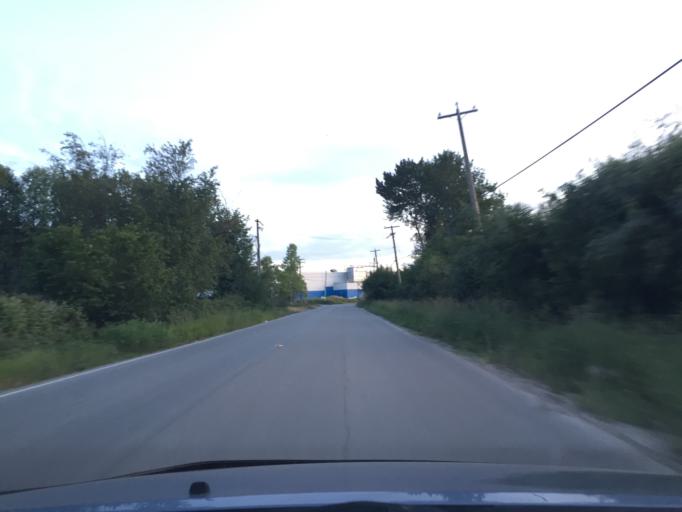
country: CA
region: British Columbia
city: Ladner
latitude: 49.1383
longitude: -123.0640
